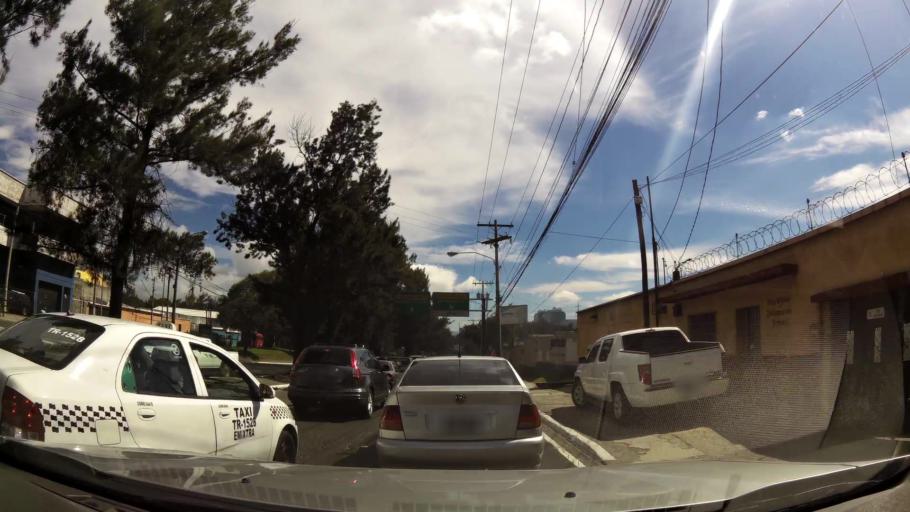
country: GT
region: Guatemala
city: Guatemala City
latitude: 14.6304
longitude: -90.5568
